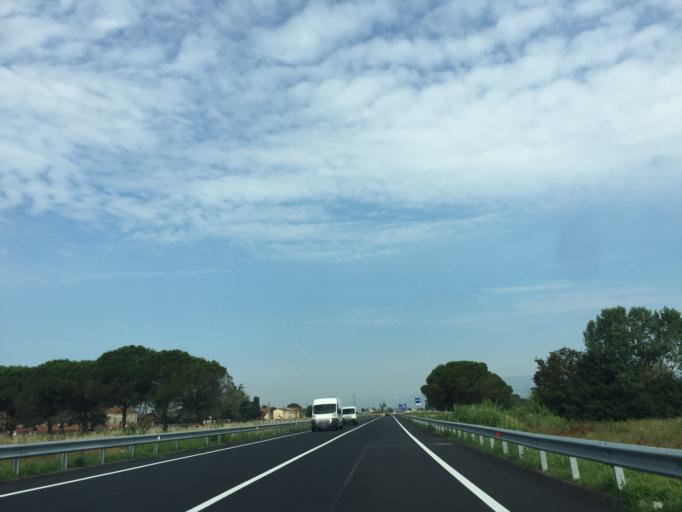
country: IT
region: Tuscany
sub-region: Provincia di Pistoia
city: Monsummano Terme
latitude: 43.8505
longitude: 10.8050
